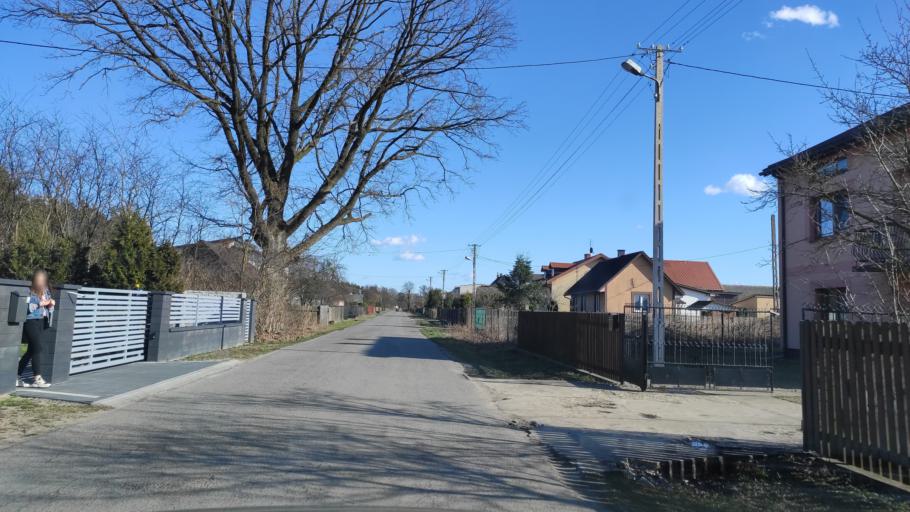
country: PL
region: Masovian Voivodeship
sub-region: Powiat radomski
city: Jastrzebia
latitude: 51.4588
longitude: 21.2618
